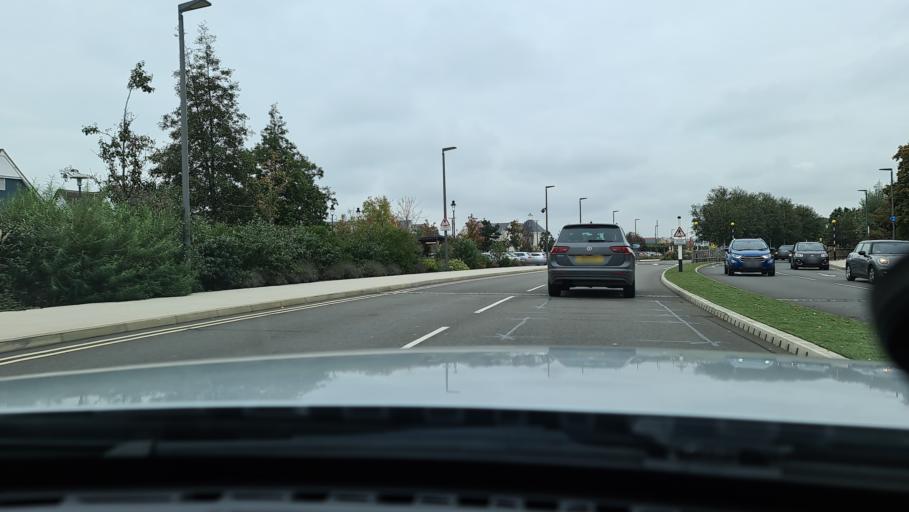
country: GB
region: England
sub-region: Oxfordshire
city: Bicester
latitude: 51.8932
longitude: -1.1568
